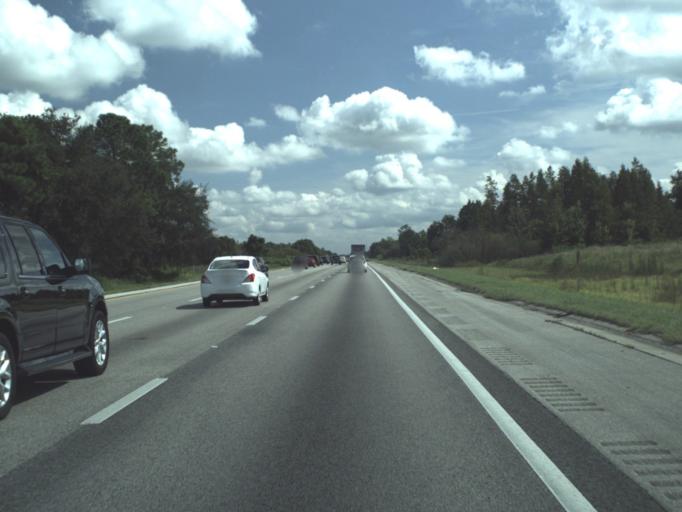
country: US
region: Florida
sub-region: Polk County
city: Lake Alfred
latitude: 28.1953
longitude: -81.7105
